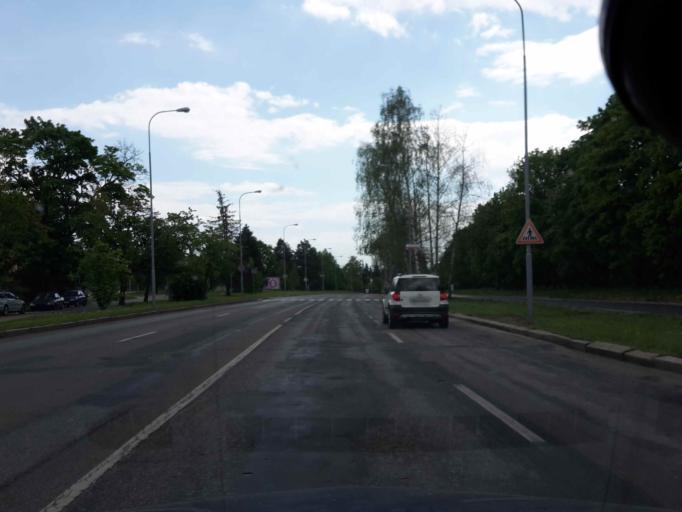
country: CZ
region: South Moravian
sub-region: Mesto Brno
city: Brno
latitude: 49.2291
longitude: 16.6312
